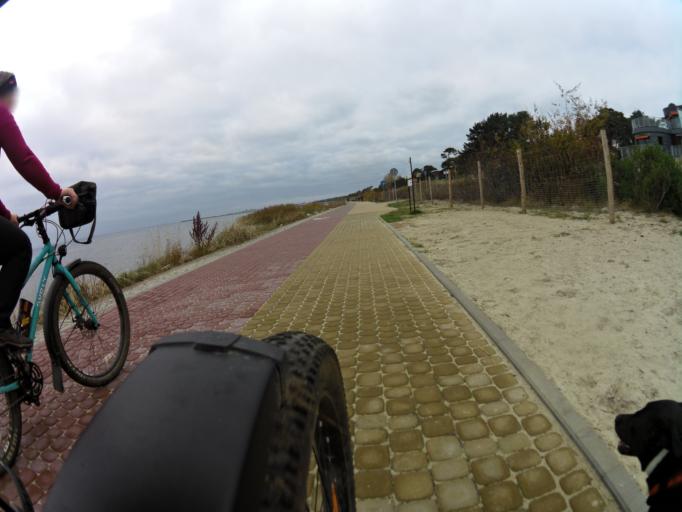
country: PL
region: Pomeranian Voivodeship
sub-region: Powiat pucki
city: Jastarnia
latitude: 54.6778
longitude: 18.7164
